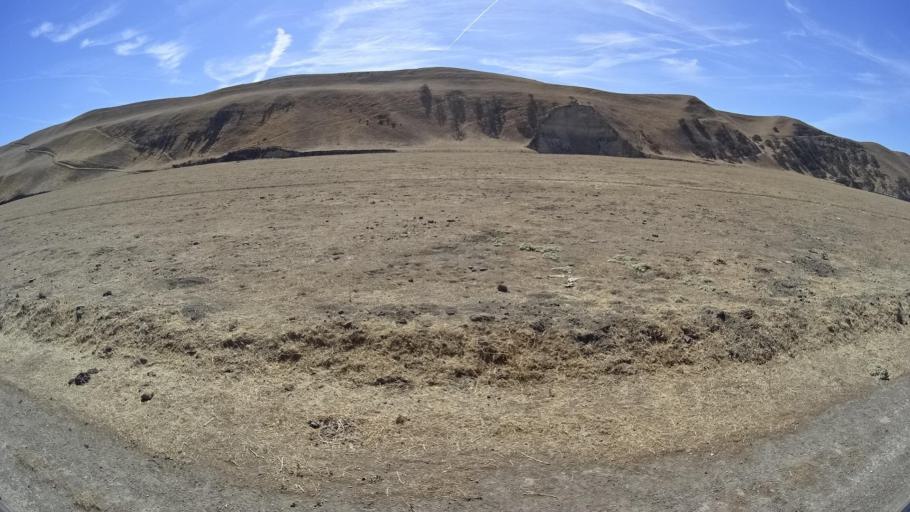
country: US
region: California
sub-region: San Luis Obispo County
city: Lake Nacimiento
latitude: 36.0325
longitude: -120.8562
